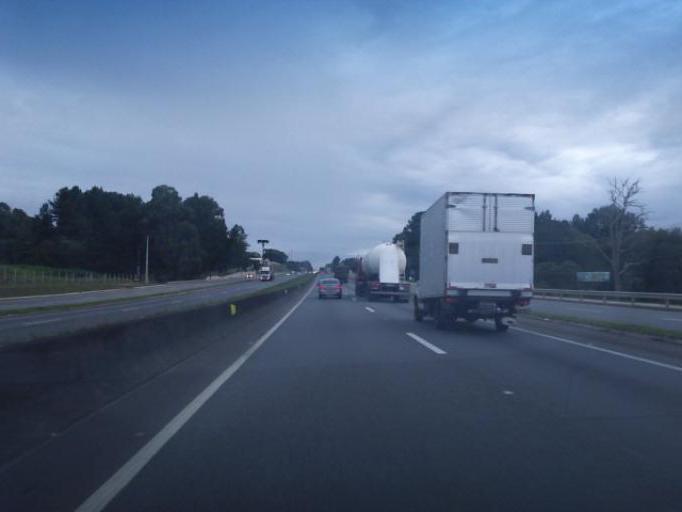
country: BR
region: Parana
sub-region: Sao Jose Dos Pinhais
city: Sao Jose dos Pinhais
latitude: -25.7029
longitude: -49.1424
